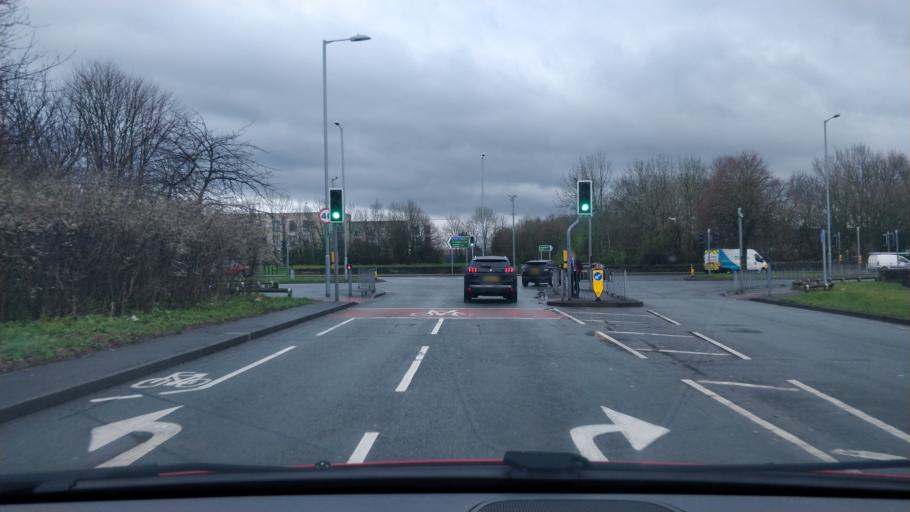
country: GB
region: England
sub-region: Knowsley
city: Huyton
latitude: 53.4211
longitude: -2.8481
